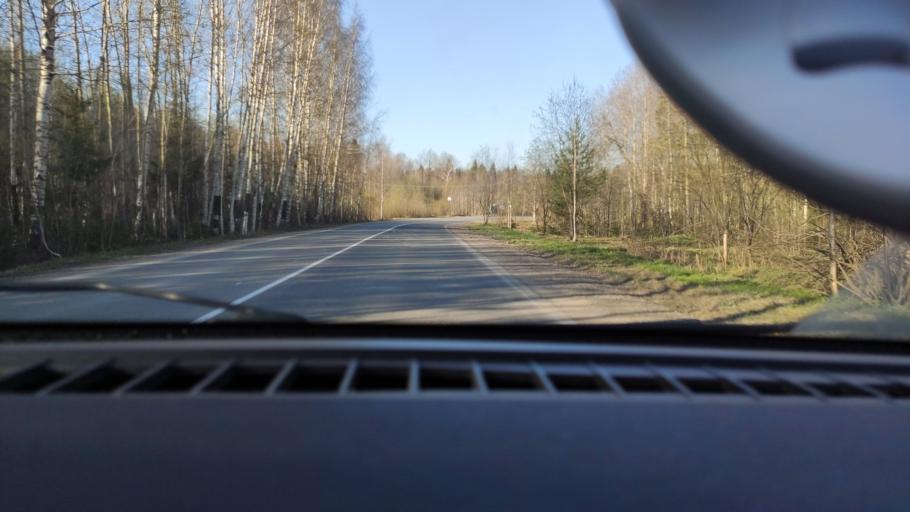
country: RU
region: Perm
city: Polazna
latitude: 58.1224
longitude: 56.4330
